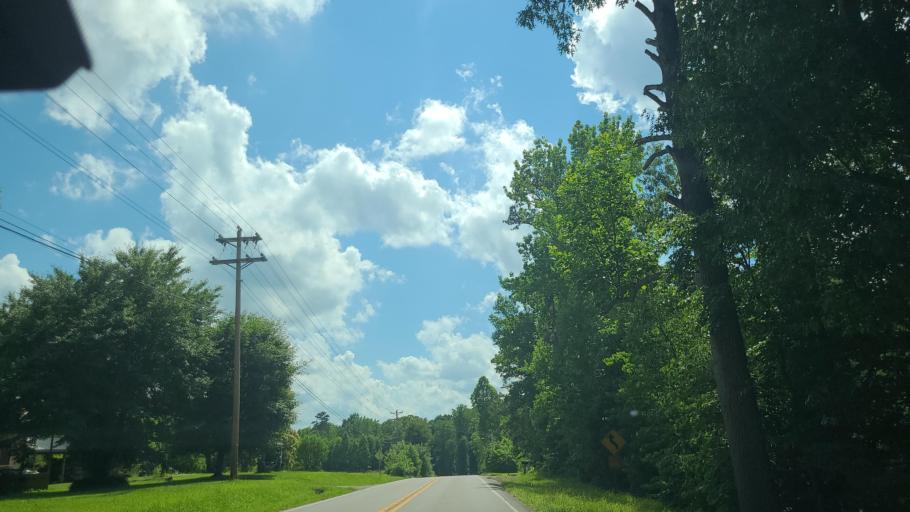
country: US
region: Kentucky
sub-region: Whitley County
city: Williamsburg
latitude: 36.8696
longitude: -84.2181
